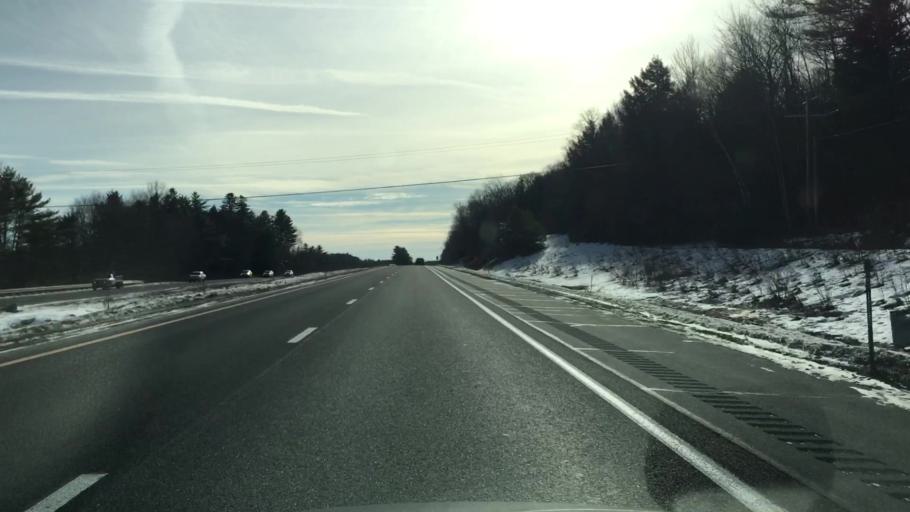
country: US
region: New Hampshire
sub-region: Sullivan County
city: Grantham
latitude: 43.5375
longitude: -72.1390
